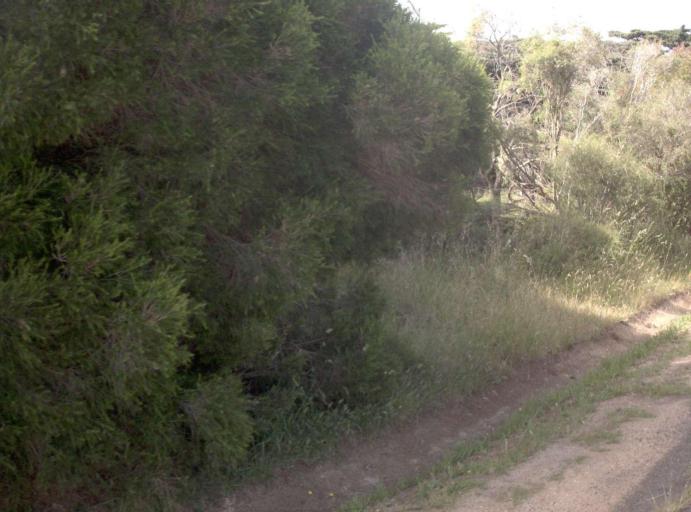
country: AU
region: Victoria
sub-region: Bass Coast
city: Phillip Island
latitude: -38.4840
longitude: 145.1741
